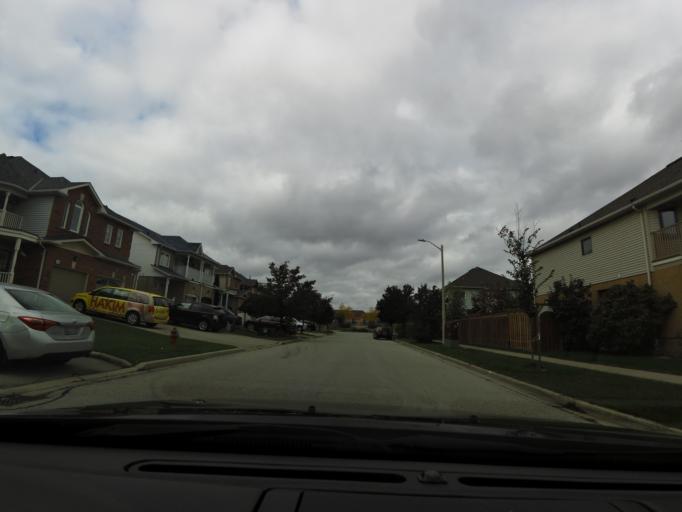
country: CA
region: Ontario
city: Burlington
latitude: 43.3923
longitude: -79.7836
